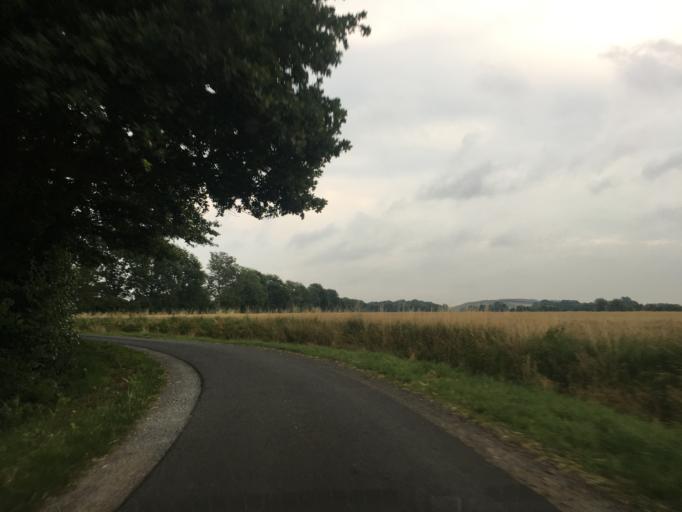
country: DE
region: North Rhine-Westphalia
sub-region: Regierungsbezirk Munster
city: Muenster
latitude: 52.0142
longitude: 7.6239
